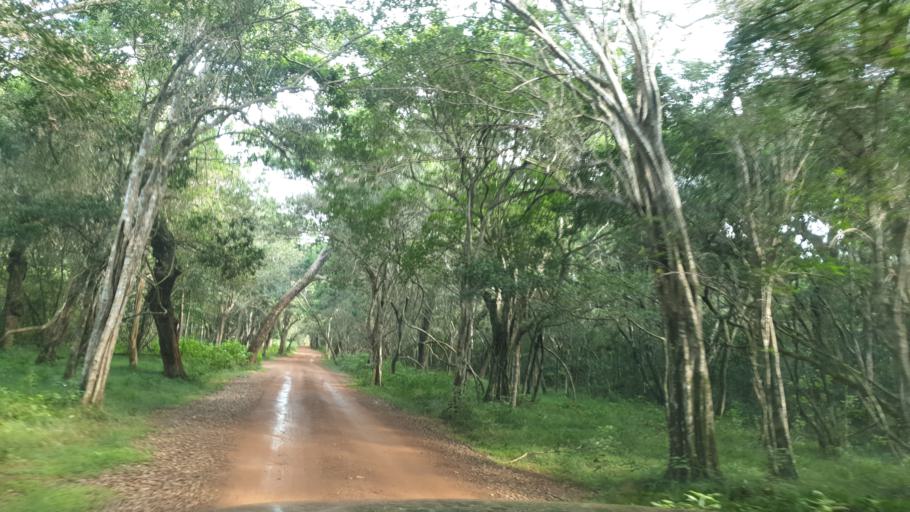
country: LK
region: North Central
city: Anuradhapura
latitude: 8.3804
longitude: 80.0654
